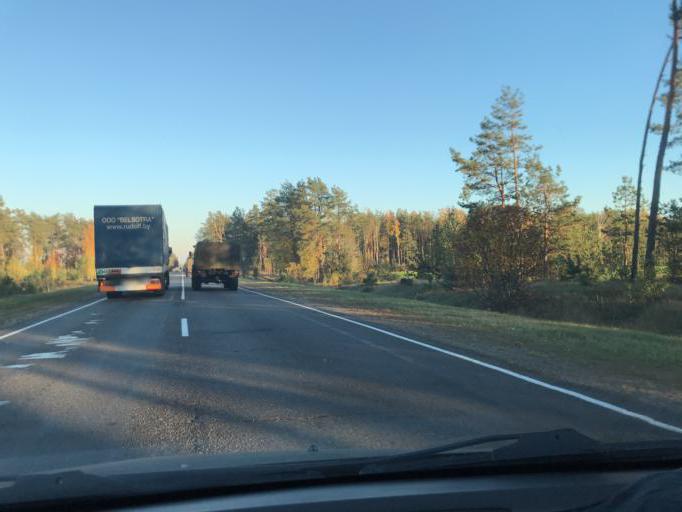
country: BY
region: Minsk
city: Staryya Darohi
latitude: 53.0481
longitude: 28.0842
